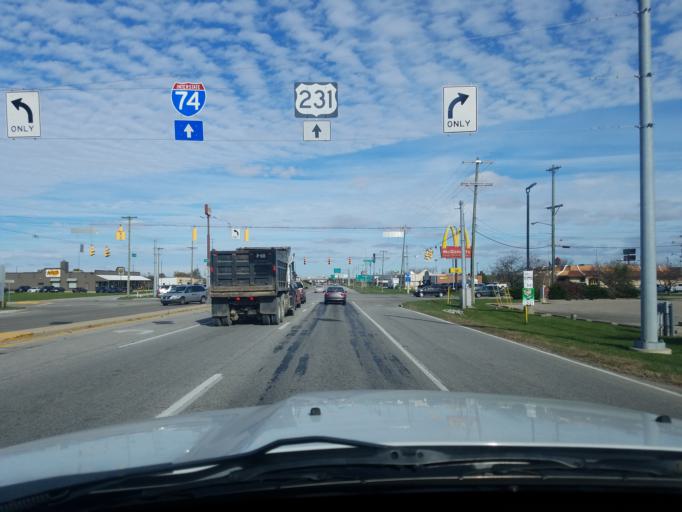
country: US
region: Indiana
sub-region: Montgomery County
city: Crawfordsville
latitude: 40.0752
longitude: -86.9054
